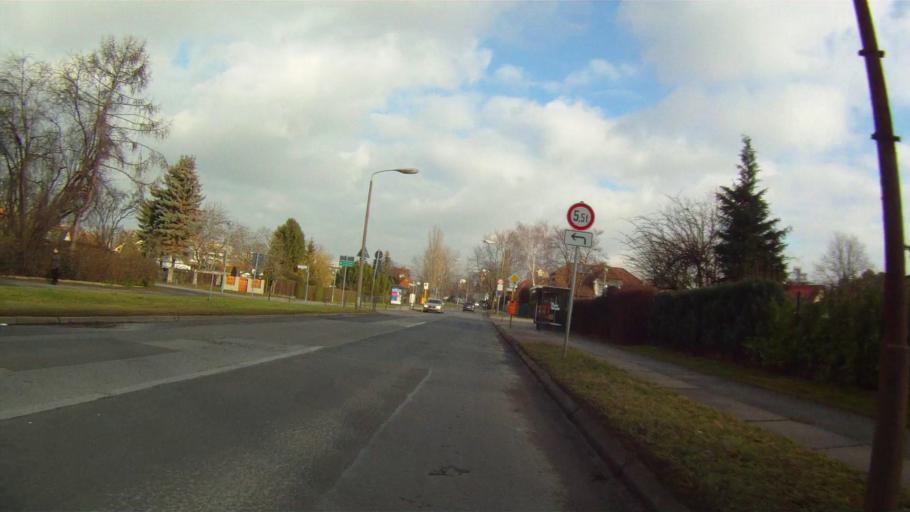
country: DE
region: Berlin
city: Biesdorf
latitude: 52.5193
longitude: 13.5305
